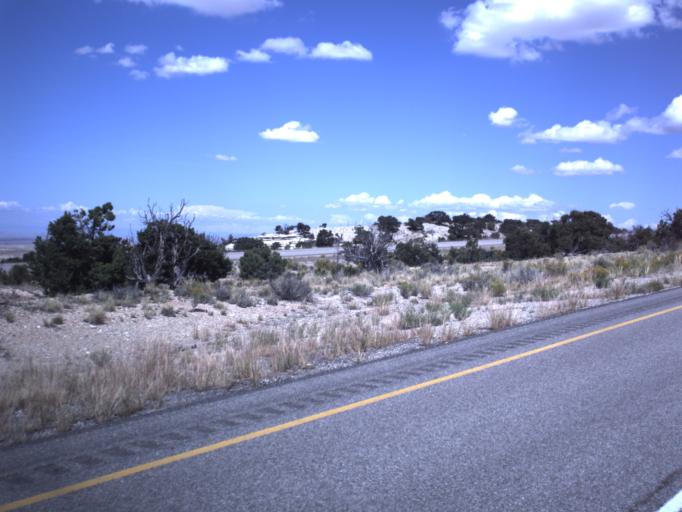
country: US
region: Utah
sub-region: Emery County
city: Ferron
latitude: 38.8432
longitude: -110.9498
